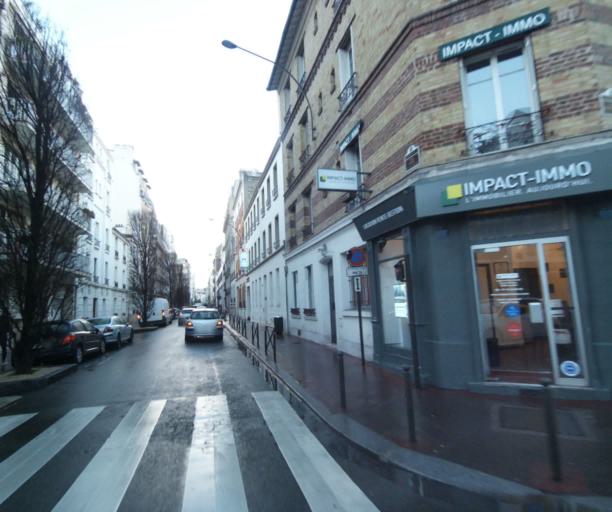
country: FR
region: Ile-de-France
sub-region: Departement des Hauts-de-Seine
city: Levallois-Perret
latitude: 48.8954
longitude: 2.2885
